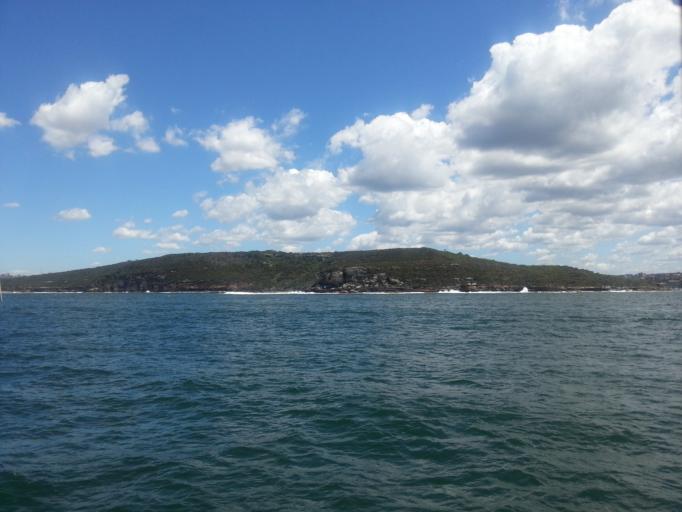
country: AU
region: New South Wales
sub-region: Manly Vale
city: Manly
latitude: -33.8154
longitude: 151.2796
